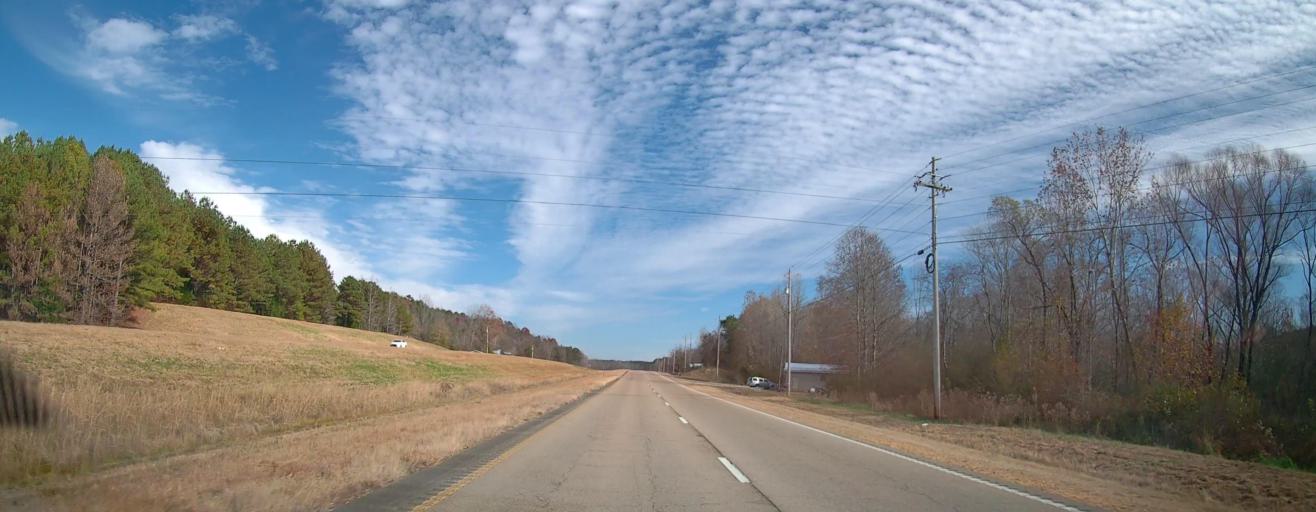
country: US
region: Mississippi
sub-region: Alcorn County
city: Corinth
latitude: 34.9333
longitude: -88.7513
